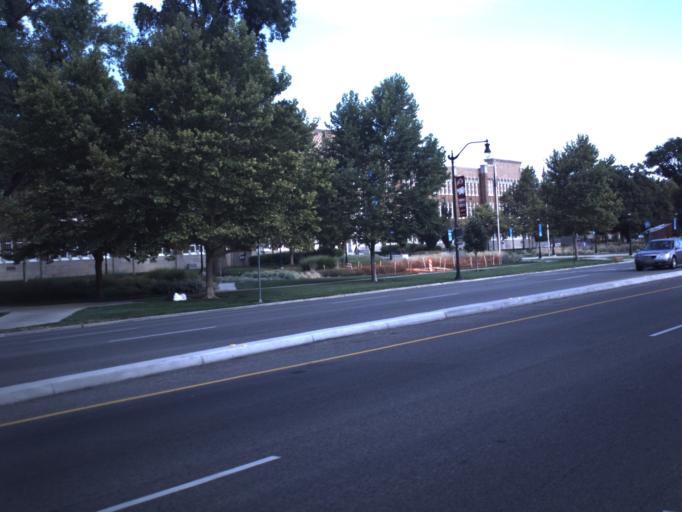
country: US
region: Utah
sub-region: Salt Lake County
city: South Salt Lake
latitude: 40.7361
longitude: -111.8884
